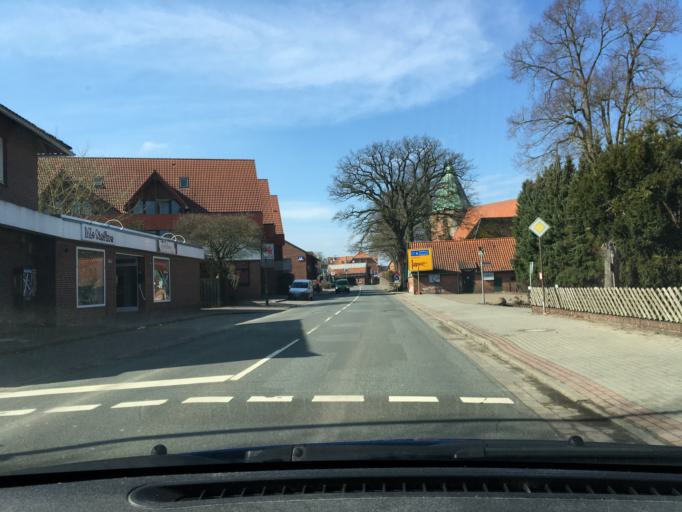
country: DE
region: Lower Saxony
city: Salzhausen
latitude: 53.2247
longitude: 10.1716
